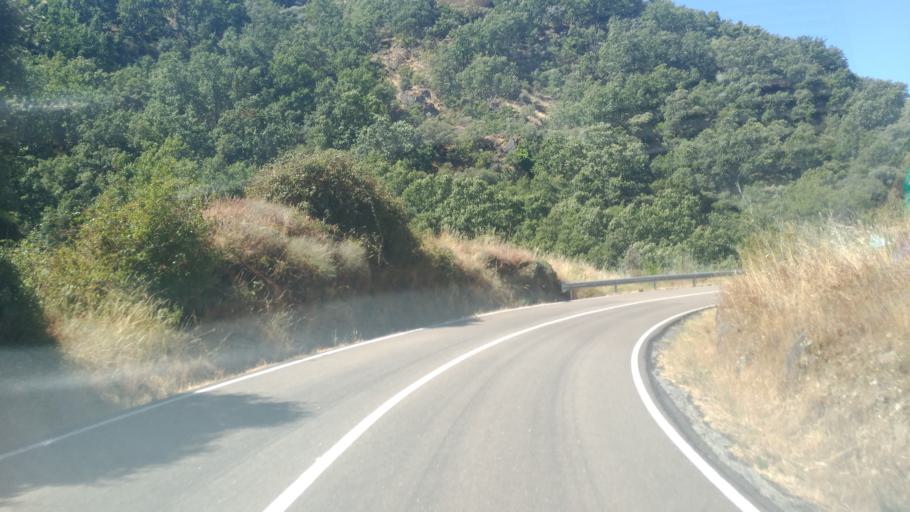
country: ES
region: Castille and Leon
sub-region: Provincia de Salamanca
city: Mieza
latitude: 41.1849
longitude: -6.6623
